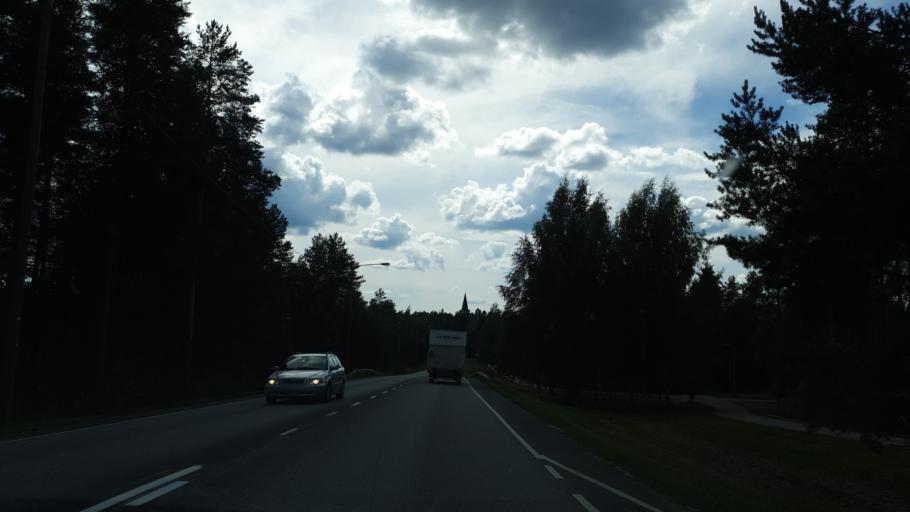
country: FI
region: Kainuu
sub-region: Kajaani
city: Sotkamo
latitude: 64.1373
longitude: 28.4118
